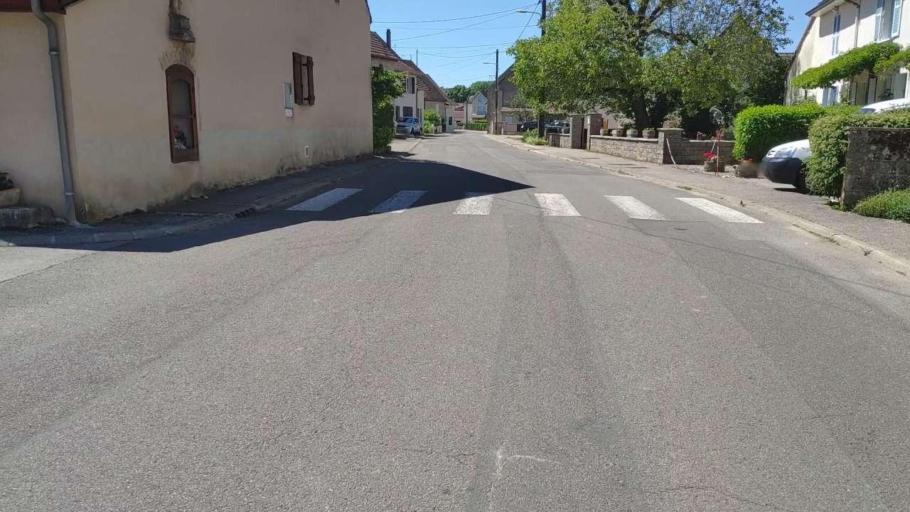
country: FR
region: Franche-Comte
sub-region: Departement du Jura
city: Perrigny
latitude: 46.7528
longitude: 5.6162
